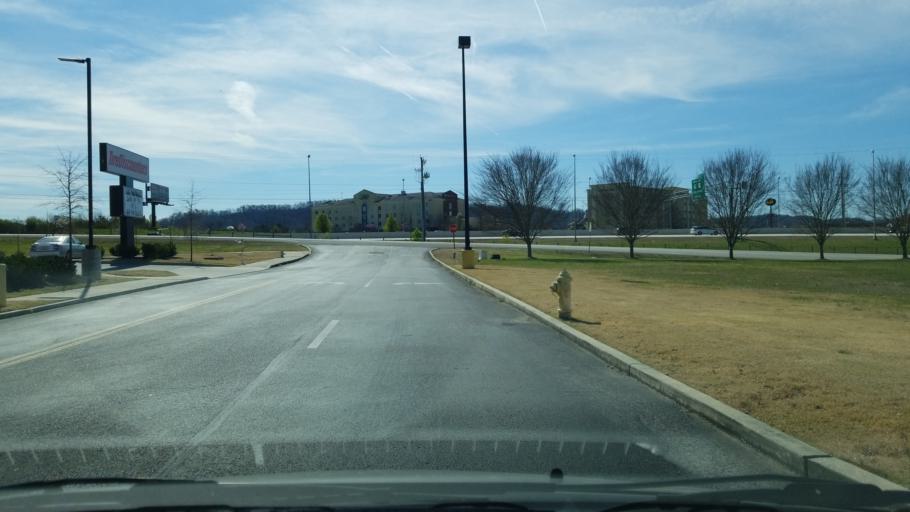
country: US
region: Tennessee
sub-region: Hamilton County
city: Collegedale
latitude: 35.0890
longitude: -85.0646
